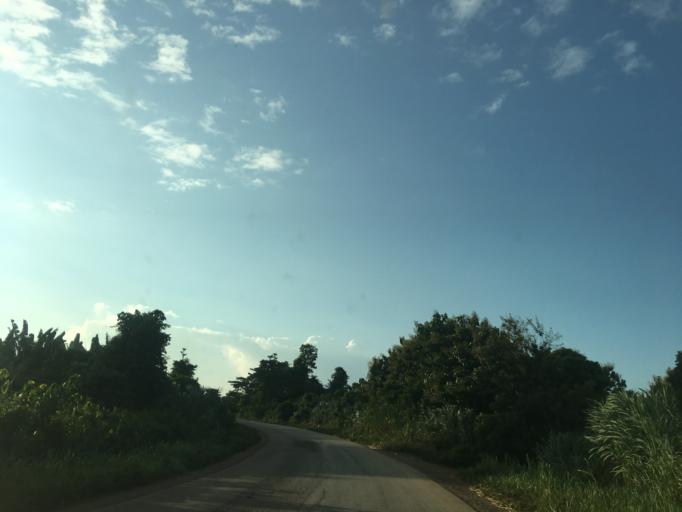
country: GH
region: Western
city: Bibiani
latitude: 6.5645
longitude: -2.3700
